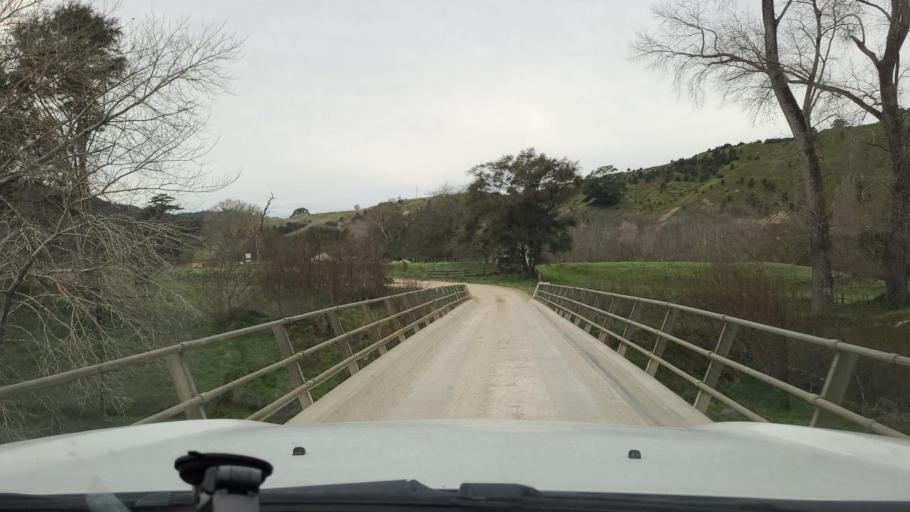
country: NZ
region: Gisborne
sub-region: Gisborne District
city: Gisborne
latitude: -38.5832
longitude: 178.0508
